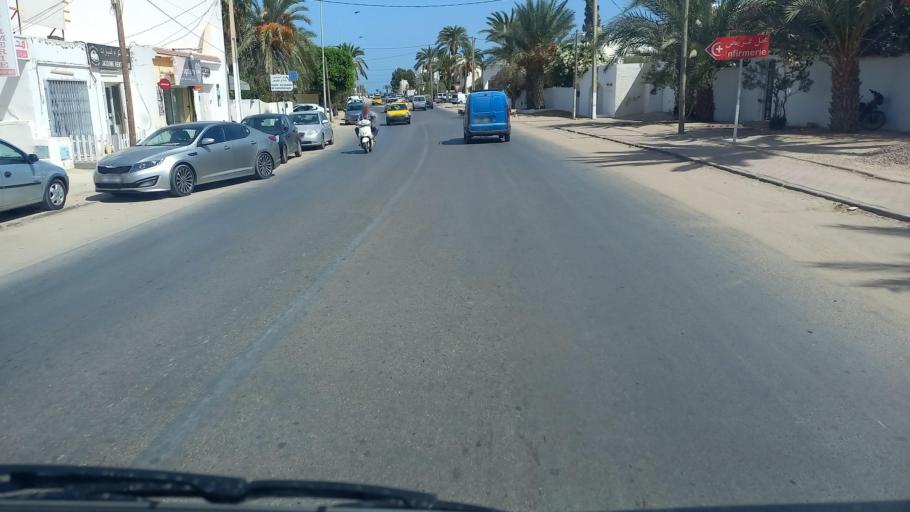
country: TN
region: Madanin
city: Houmt Souk
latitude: 33.8728
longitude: 10.8739
